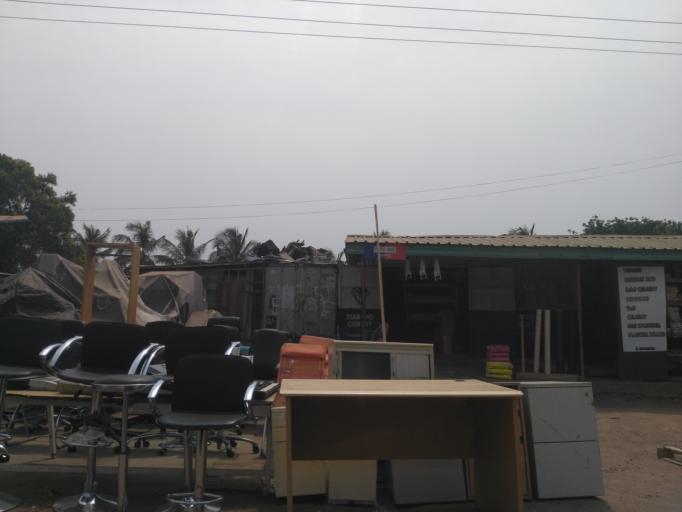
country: GH
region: Greater Accra
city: Nungua
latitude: 5.5949
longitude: -0.0874
